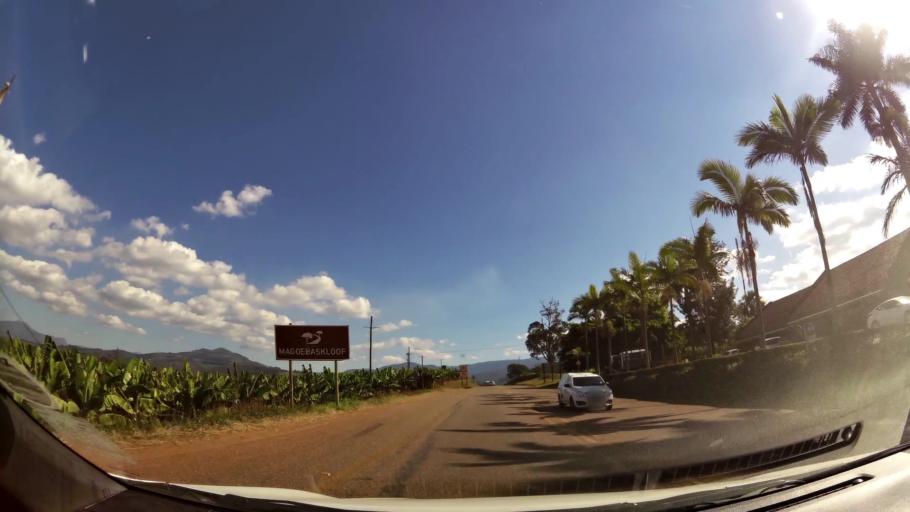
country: ZA
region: Limpopo
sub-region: Mopani District Municipality
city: Tzaneen
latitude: -23.8027
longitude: 30.1221
